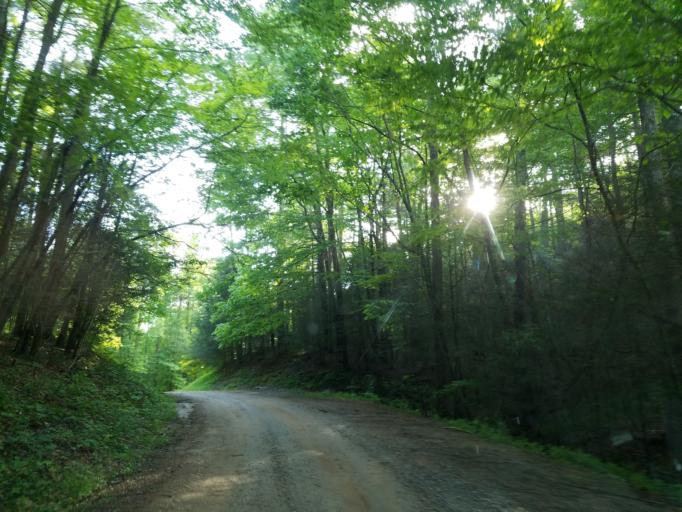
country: US
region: Georgia
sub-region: Union County
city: Blairsville
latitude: 34.7470
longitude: -84.0361
